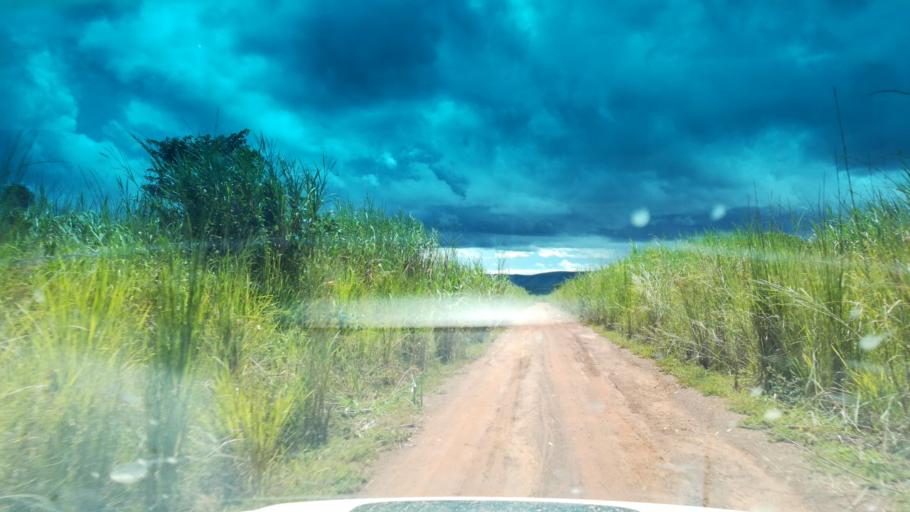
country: ZM
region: Northern
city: Kaputa
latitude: -7.7389
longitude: 29.2487
